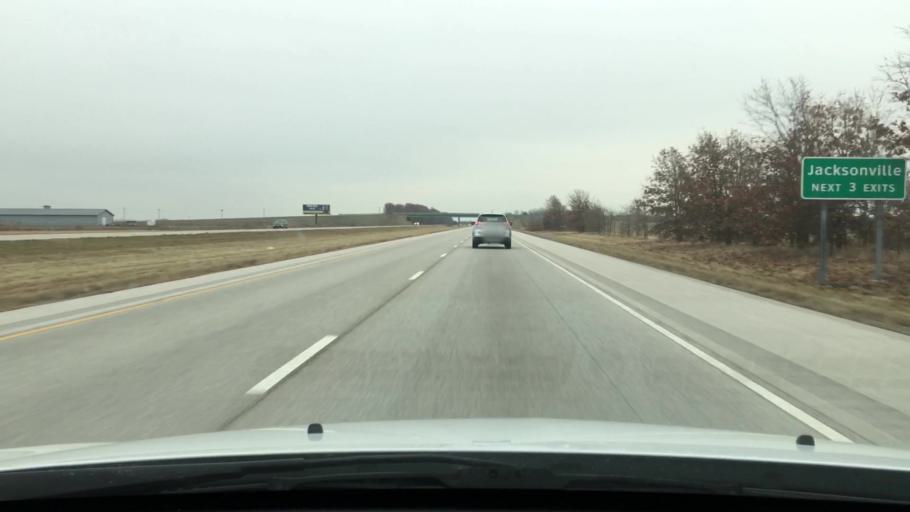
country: US
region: Illinois
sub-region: Morgan County
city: South Jacksonville
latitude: 39.6801
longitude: -90.3325
